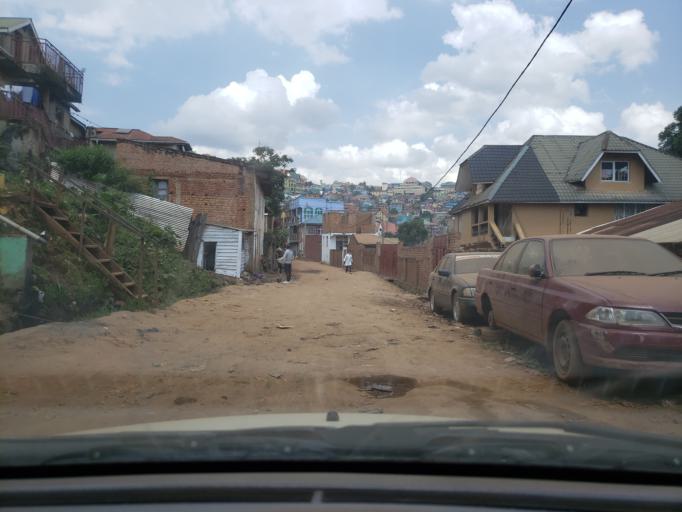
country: CD
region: South Kivu
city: Bukavu
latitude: -2.4959
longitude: 28.8584
